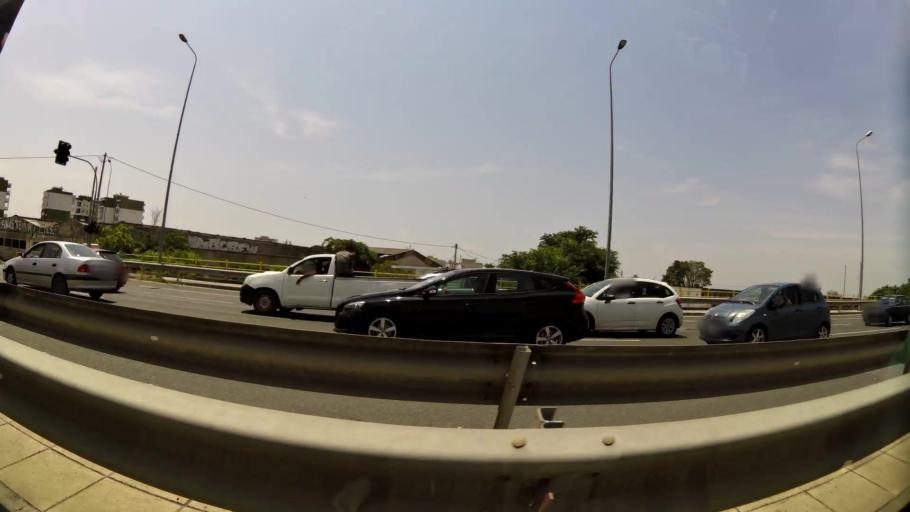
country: GR
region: Central Macedonia
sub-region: Nomos Thessalonikis
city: Ampelokipoi
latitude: 40.6474
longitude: 22.9141
